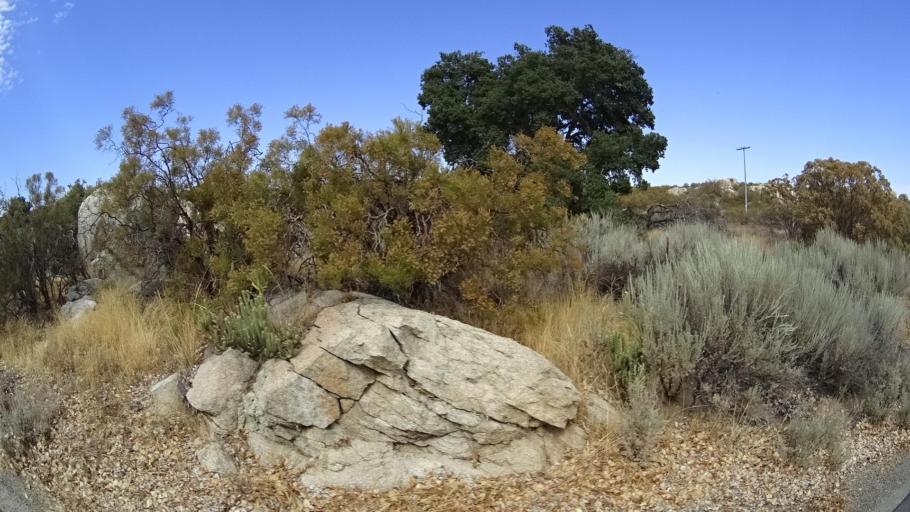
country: MX
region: Baja California
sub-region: Tecate
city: Cereso del Hongo
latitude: 32.6459
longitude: -116.2864
